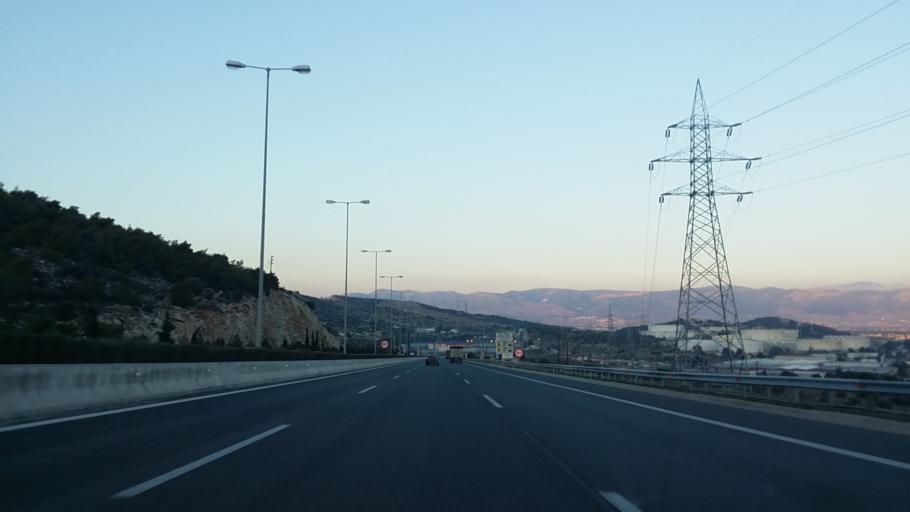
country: GR
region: Attica
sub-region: Nomarchia Dytikis Attikis
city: Mandra
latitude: 38.0331
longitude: 23.4901
